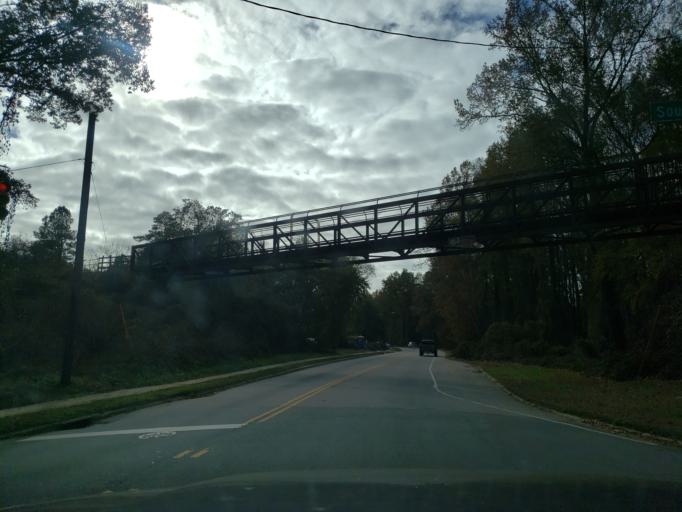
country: US
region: North Carolina
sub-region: Durham County
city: Durham
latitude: 35.9758
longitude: -78.9083
